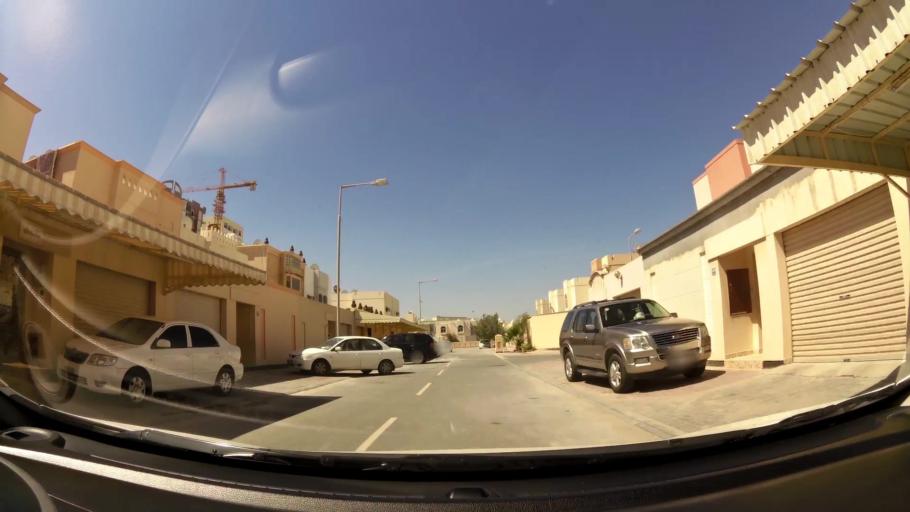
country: BH
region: Muharraq
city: Al Muharraq
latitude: 26.2672
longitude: 50.5985
